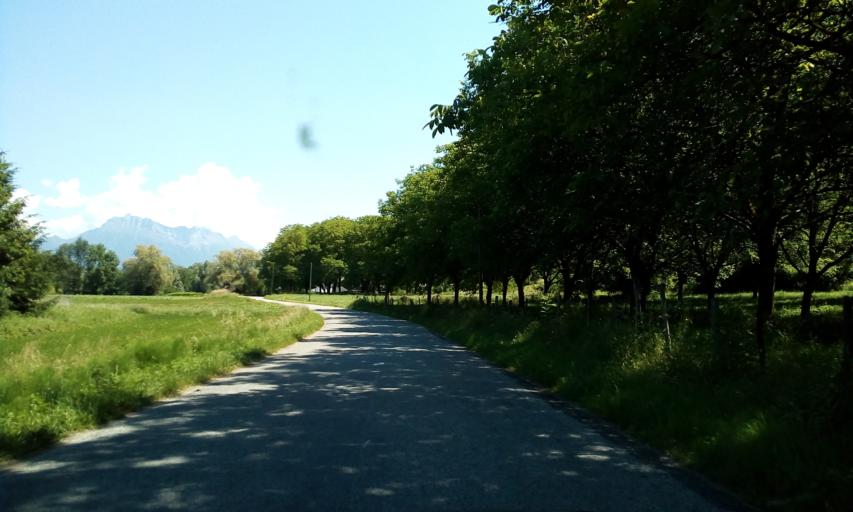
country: FR
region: Rhone-Alpes
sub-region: Departement de la Savoie
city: Montmelian
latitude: 45.4725
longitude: 6.0689
